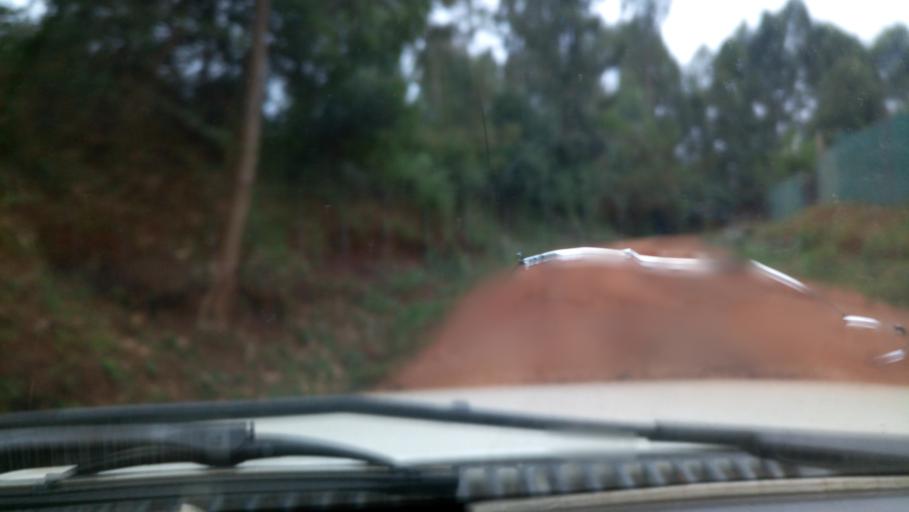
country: KE
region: Murang'a District
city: Kangema
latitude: -0.6749
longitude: 36.9759
